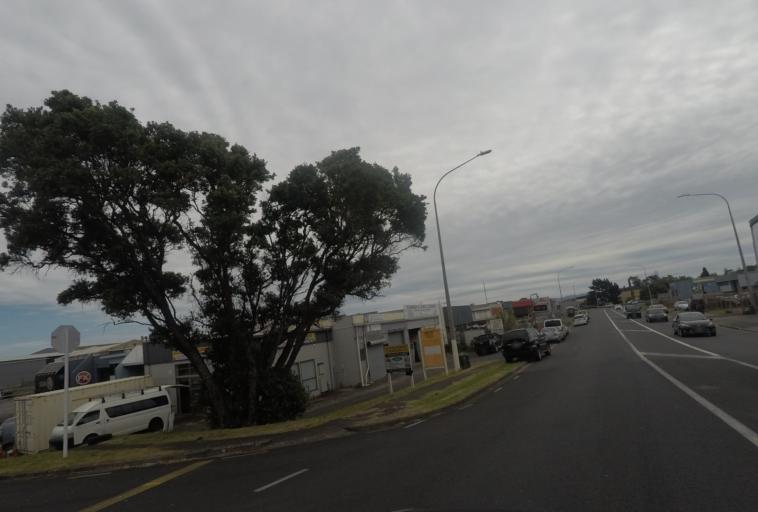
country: NZ
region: Auckland
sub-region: Auckland
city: Mangere
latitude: -36.9494
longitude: 174.8329
